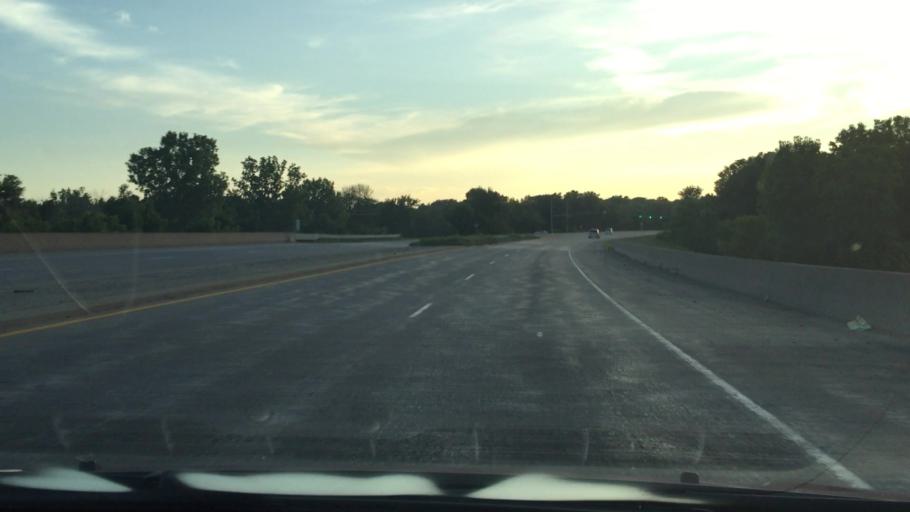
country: US
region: Iowa
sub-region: Muscatine County
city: Muscatine
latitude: 41.4521
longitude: -91.0385
